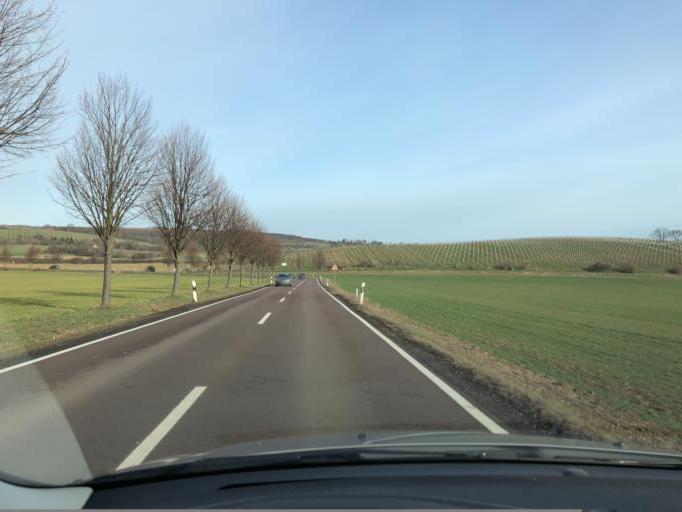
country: DE
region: Saxony-Anhalt
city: Freyburg
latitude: 51.2003
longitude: 11.7981
